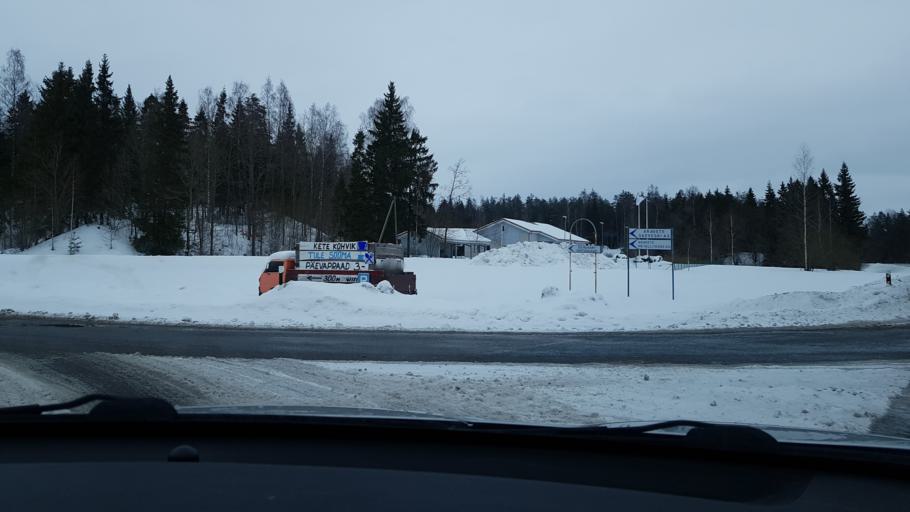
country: EE
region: Jaervamaa
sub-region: Jaerva-Jaani vald
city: Jarva-Jaani
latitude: 59.1282
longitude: 25.7467
